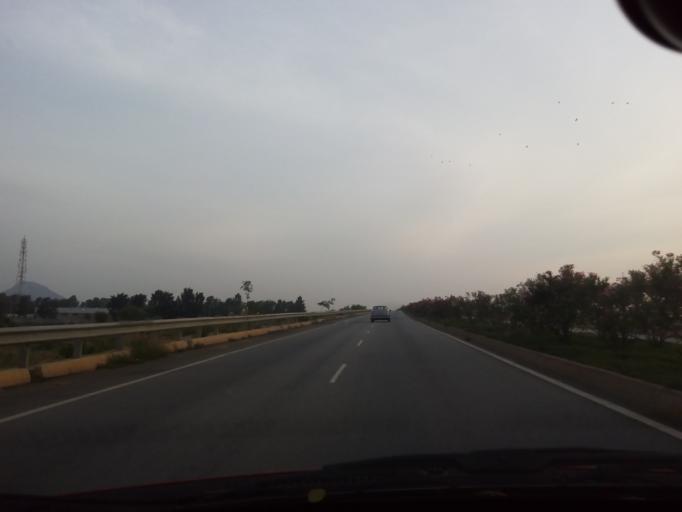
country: IN
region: Karnataka
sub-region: Chikkaballapur
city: Chik Ballapur
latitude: 13.3492
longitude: 77.7256
